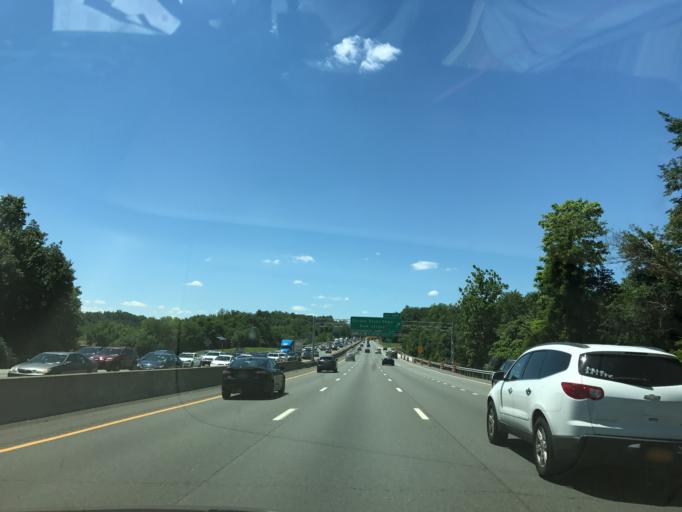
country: US
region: New York
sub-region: Rockland County
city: Spring Valley
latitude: 41.1019
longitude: -74.0302
